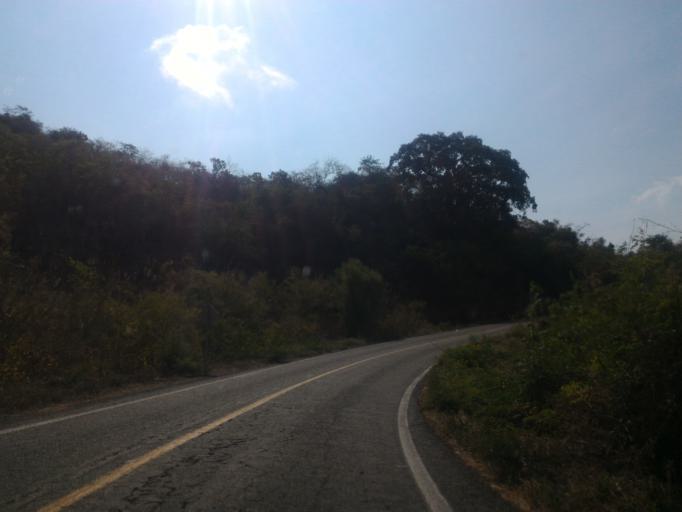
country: MX
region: Michoacan
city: Coahuayana Viejo
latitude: 18.4778
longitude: -103.5611
